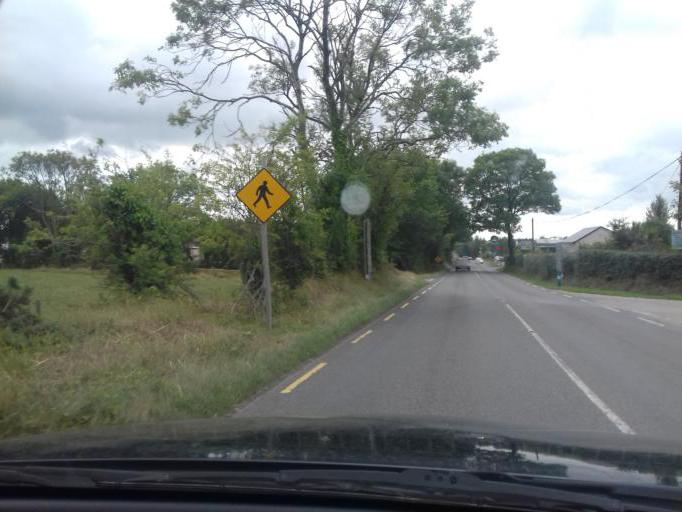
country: IE
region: Leinster
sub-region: Loch Garman
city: Ballinroad
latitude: 52.4549
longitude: -6.4005
